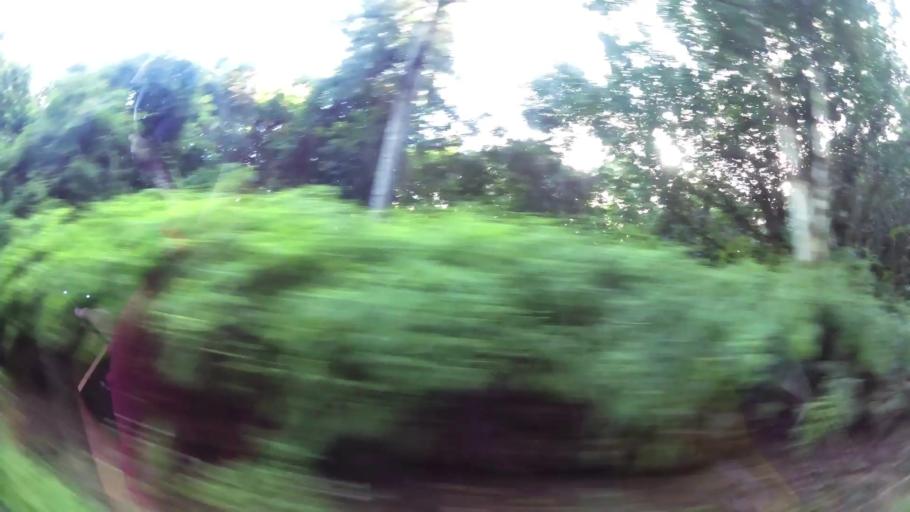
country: GP
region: Guadeloupe
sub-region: Guadeloupe
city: Bouillante
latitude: 16.1758
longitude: -61.6992
